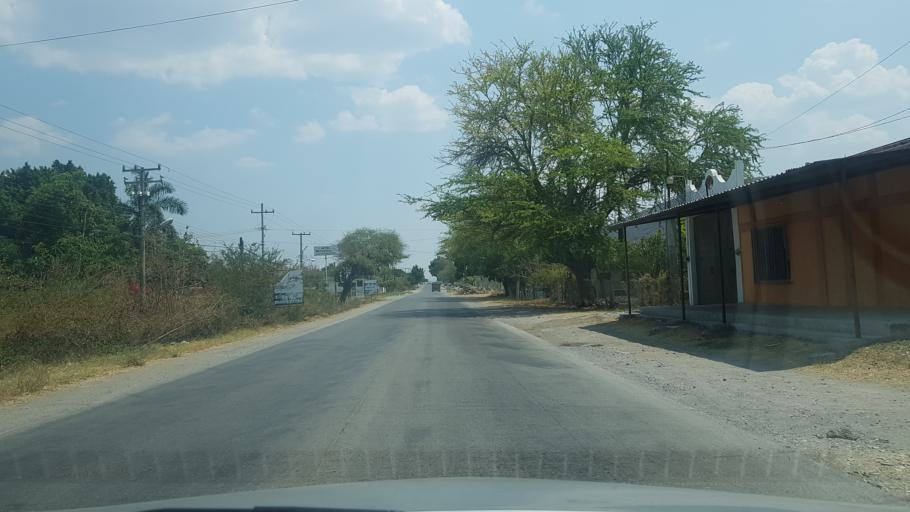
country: MX
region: Morelos
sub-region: Tlaltizapan de Zapata
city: Colonia Palo Prieto (Chipitongo)
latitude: 18.7255
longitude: -99.1229
